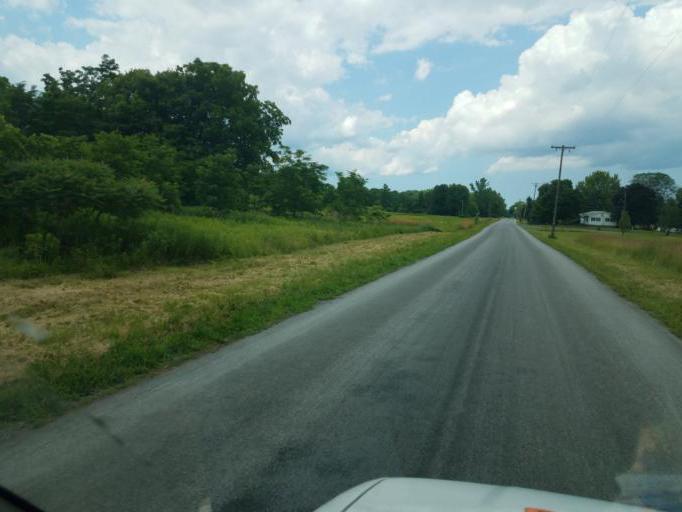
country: US
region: New York
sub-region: Wayne County
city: Clyde
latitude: 43.0424
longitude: -76.8835
